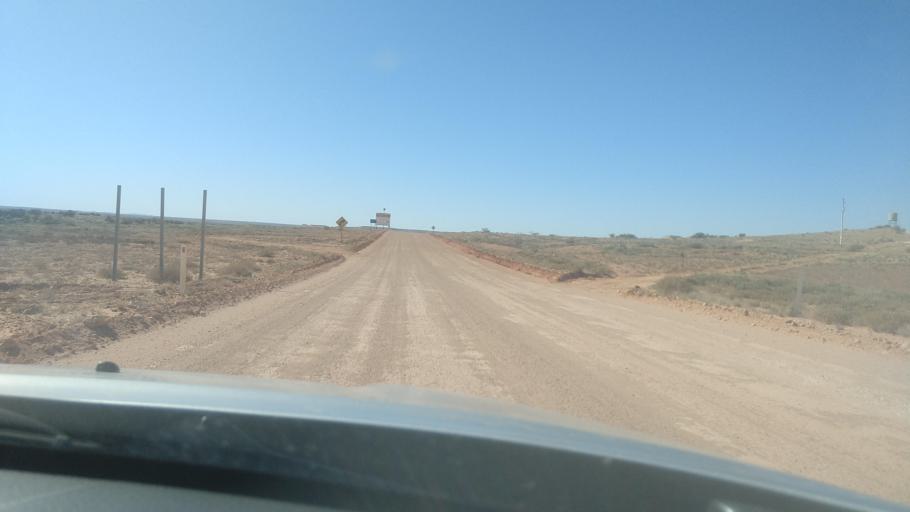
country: AU
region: South Australia
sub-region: Coober Pedy
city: Coober Pedy
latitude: -29.0343
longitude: 134.8055
